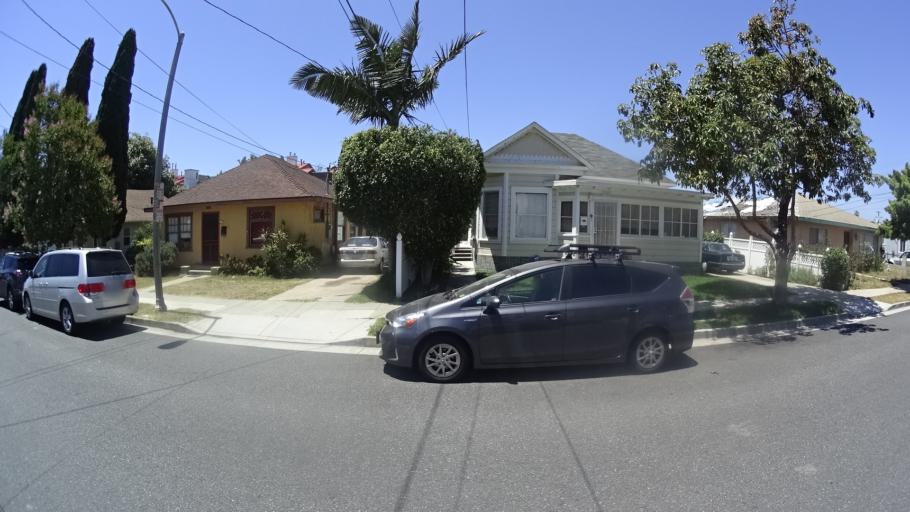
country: US
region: California
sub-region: Los Angeles County
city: Santa Monica
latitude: 34.0227
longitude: -118.4695
